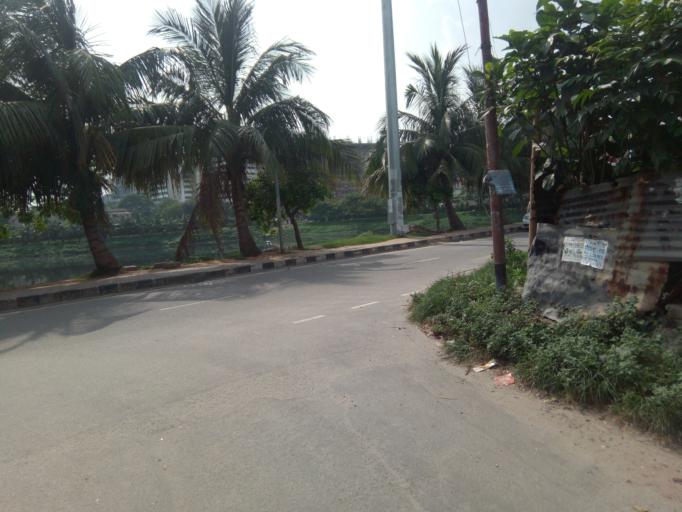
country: BD
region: Dhaka
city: Paltan
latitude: 23.7496
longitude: 90.3975
